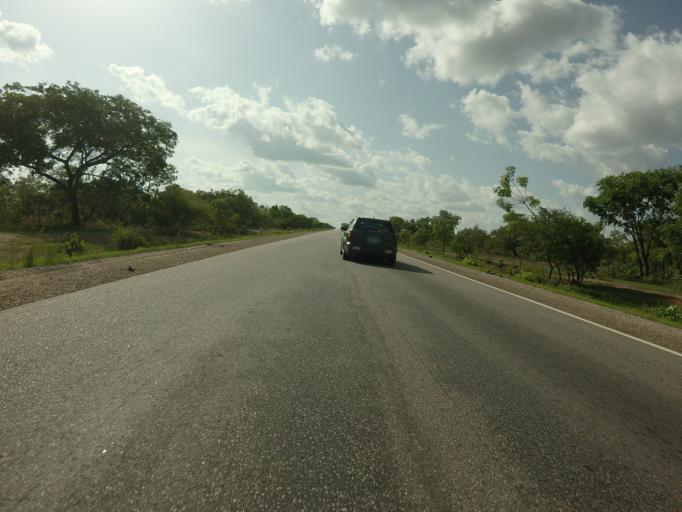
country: GH
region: Upper East
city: Bolgatanga
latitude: 10.5306
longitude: -0.8182
